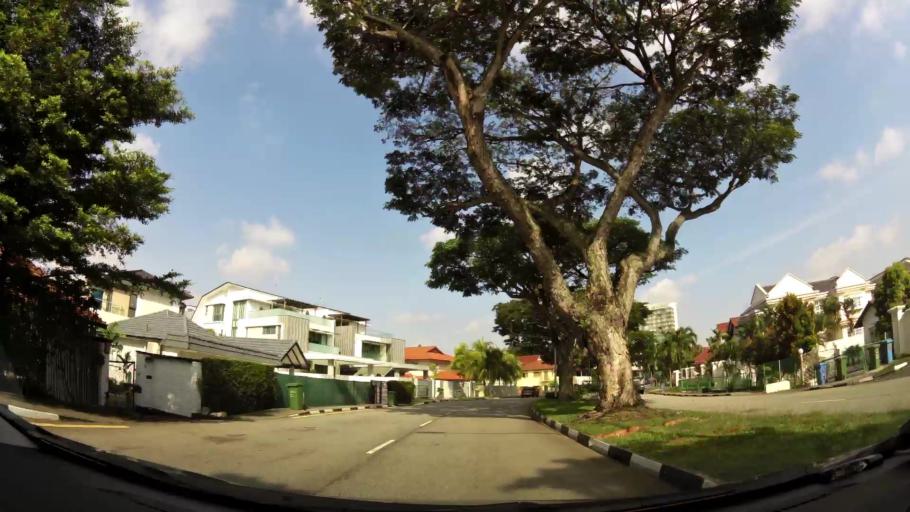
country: SG
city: Singapore
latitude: 1.3177
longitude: 103.9151
